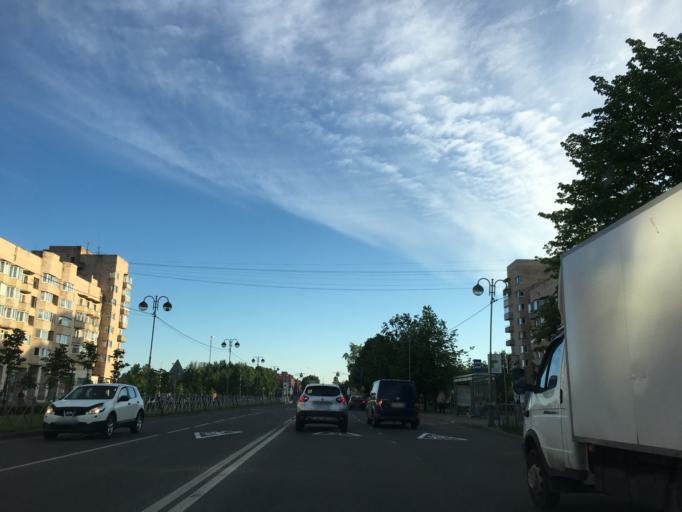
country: RU
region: Leningrad
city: Gatchina
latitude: 59.5783
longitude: 30.1353
